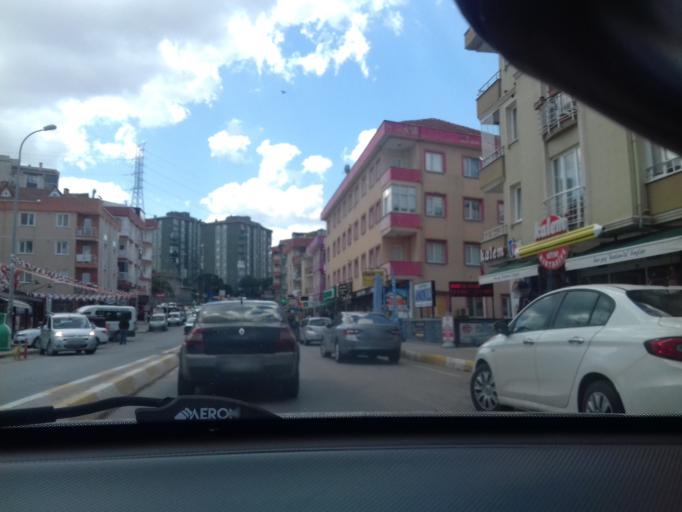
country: TR
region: Istanbul
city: Pendik
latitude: 40.9165
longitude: 29.2857
